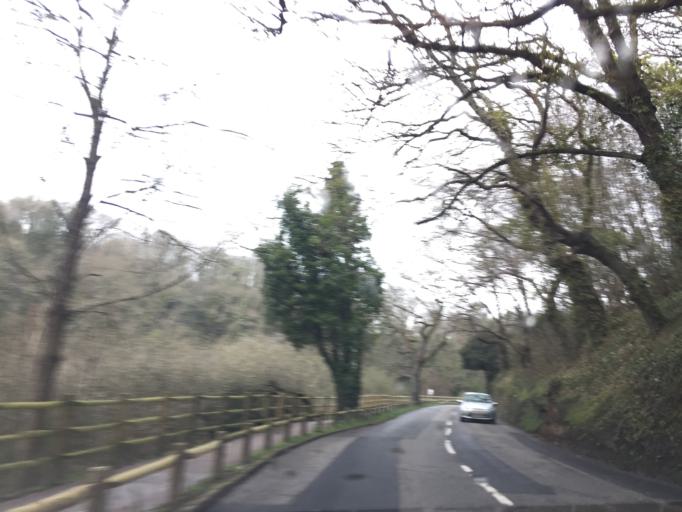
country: JE
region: St Helier
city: Saint Helier
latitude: 49.2059
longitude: -2.1569
